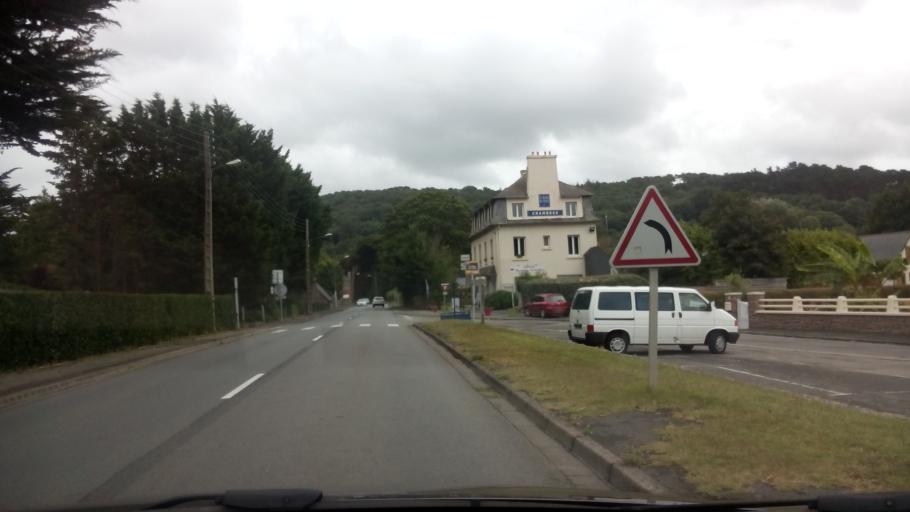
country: FR
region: Brittany
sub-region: Departement des Cotes-d'Armor
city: Plestin-les-Greves
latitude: 48.6687
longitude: -3.5988
